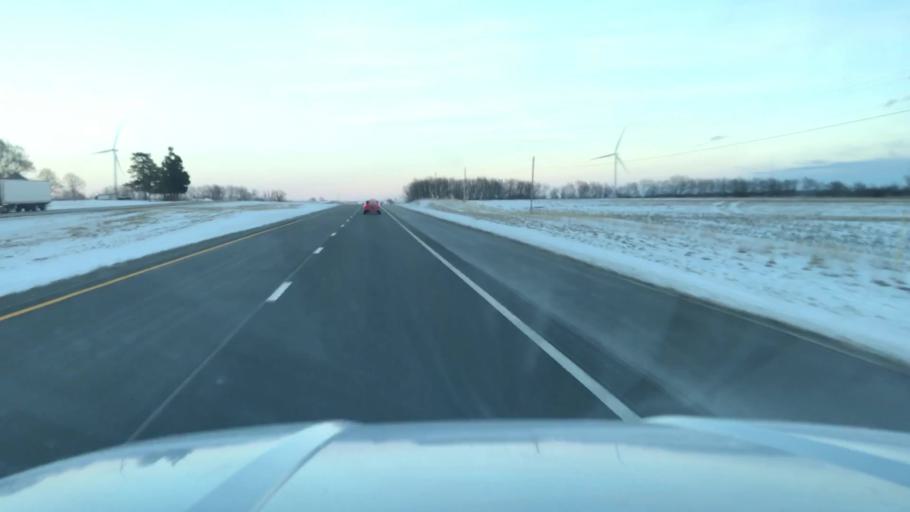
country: US
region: Missouri
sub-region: DeKalb County
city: Maysville
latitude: 39.7614
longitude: -94.3915
